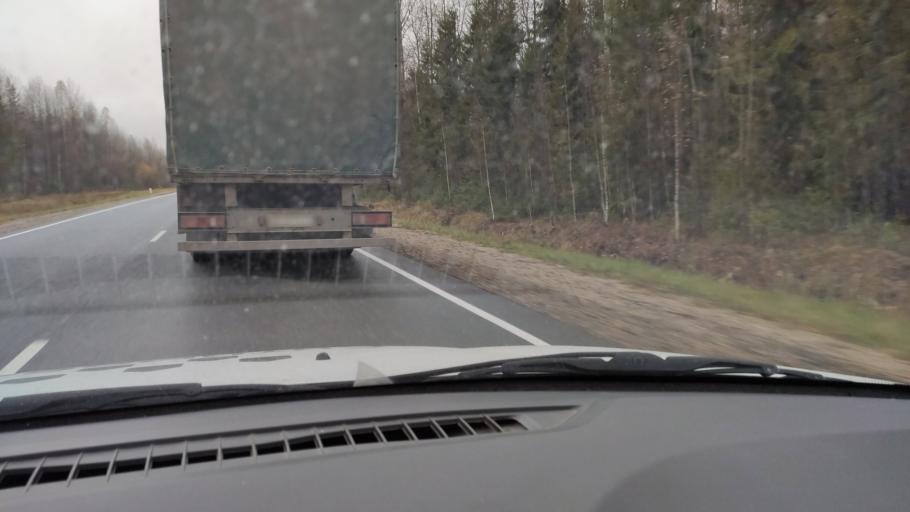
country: RU
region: Kirov
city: Chernaya Kholunitsa
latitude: 58.8016
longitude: 51.8594
